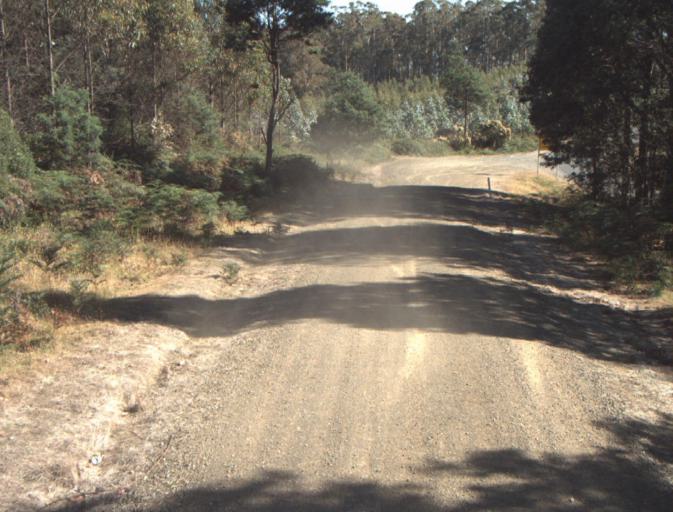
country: AU
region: Tasmania
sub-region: Dorset
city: Scottsdale
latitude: -41.2696
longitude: 147.3763
